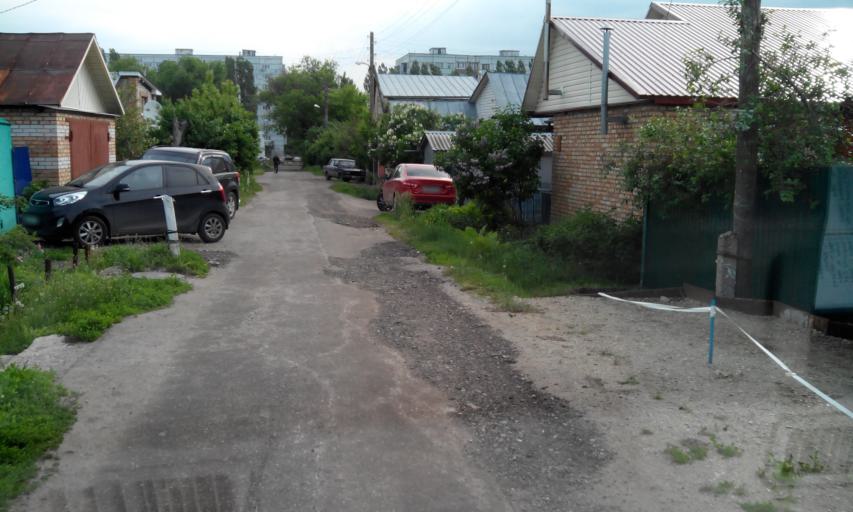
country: RU
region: Penza
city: Penza
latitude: 53.2093
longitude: 44.9695
